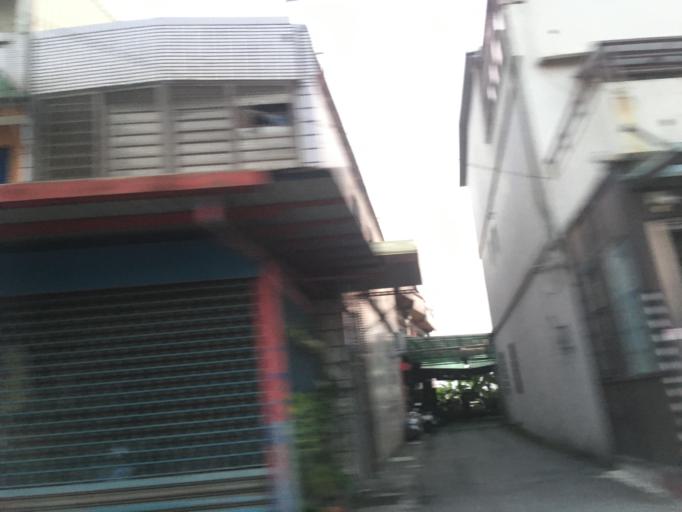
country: TW
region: Taiwan
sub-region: Yilan
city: Yilan
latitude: 24.6920
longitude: 121.7827
